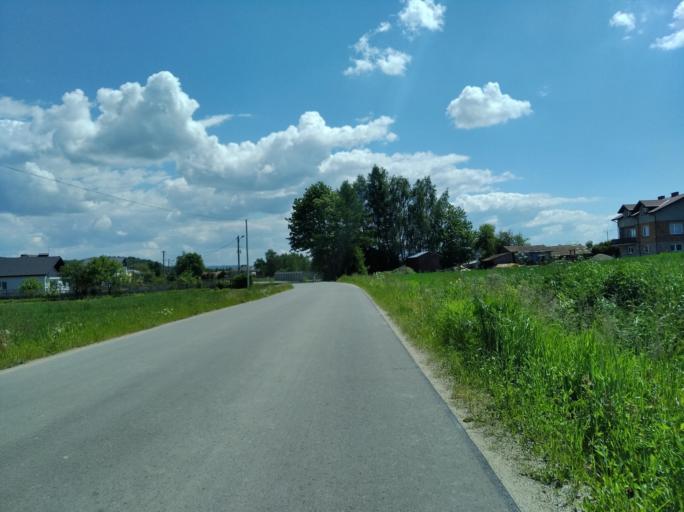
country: PL
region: Subcarpathian Voivodeship
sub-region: Powiat jasielski
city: Tarnowiec
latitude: 49.7663
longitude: 21.6121
